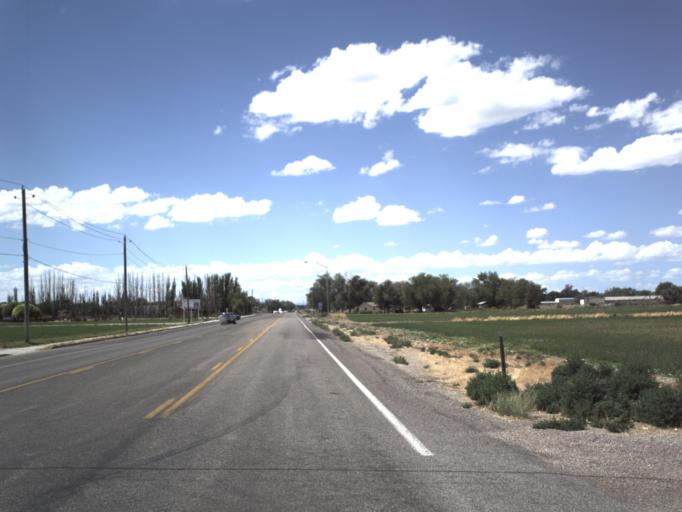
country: US
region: Utah
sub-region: Millard County
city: Delta
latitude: 39.3526
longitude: -112.5552
